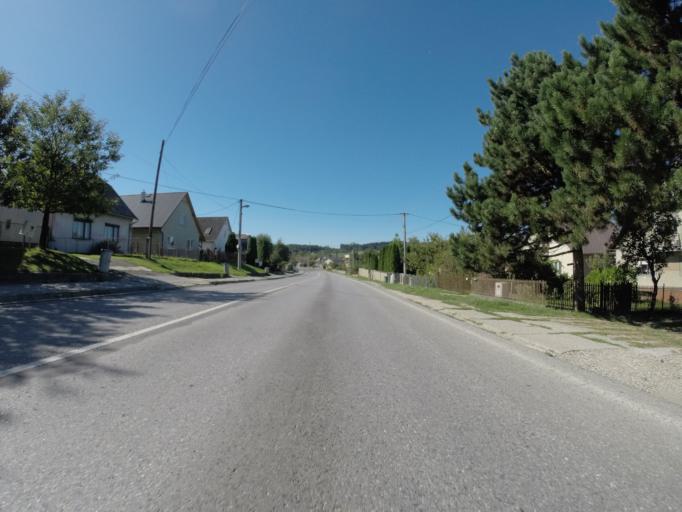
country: SK
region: Trenciansky
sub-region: Okres Povazska Bystrica
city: Povazska Bystrica
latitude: 49.0848
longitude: 18.4101
